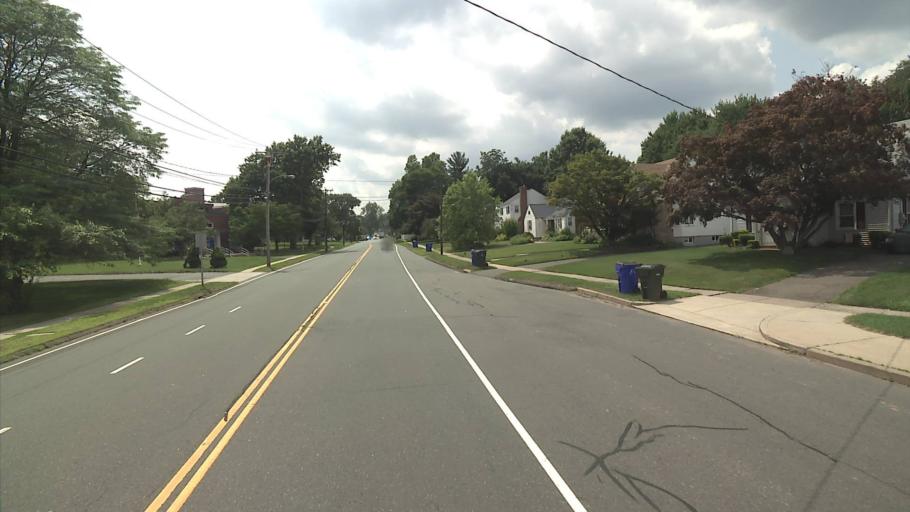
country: US
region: Connecticut
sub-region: Hartford County
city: Wethersfield
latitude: 41.6942
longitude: -72.6683
